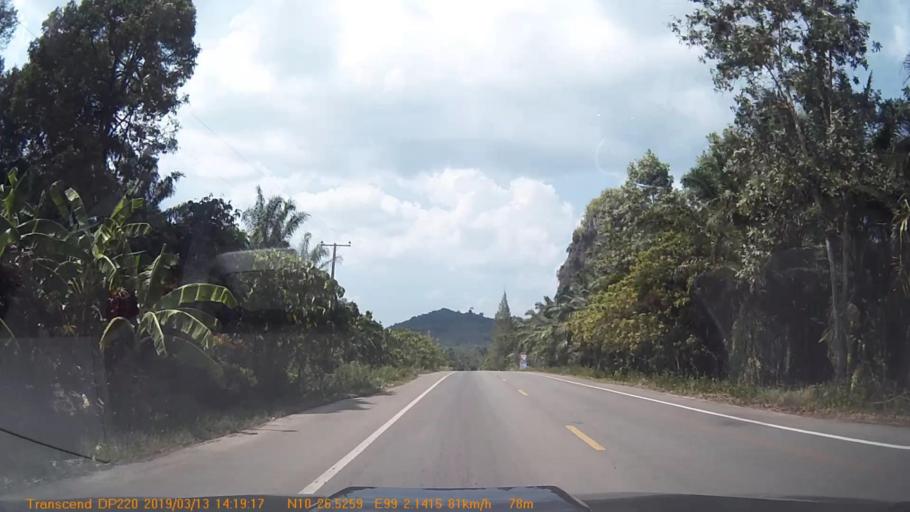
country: TH
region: Chumphon
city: Chumphon
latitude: 10.4426
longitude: 99.0355
